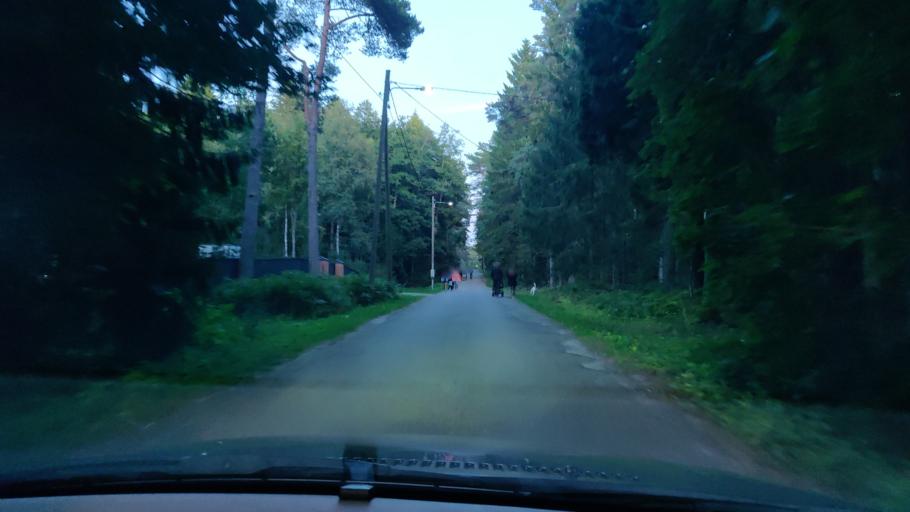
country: EE
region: Harju
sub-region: Keila linn
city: Keila
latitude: 59.3464
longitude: 24.2615
